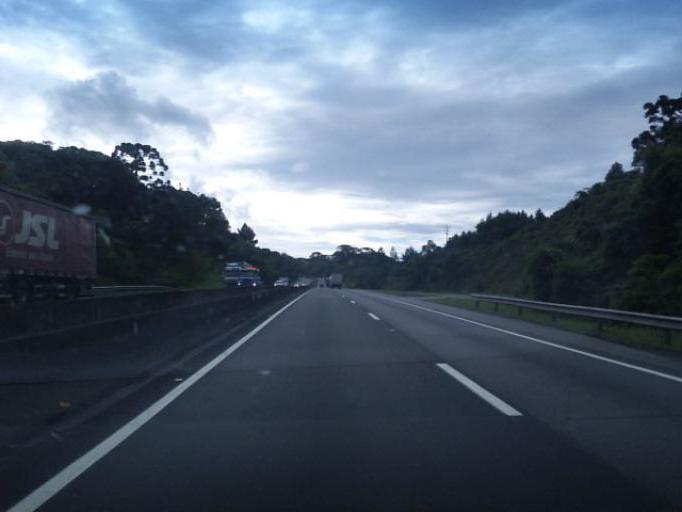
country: BR
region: Parana
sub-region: Campina Grande Do Sul
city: Campina Grande do Sul
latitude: -25.3069
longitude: -48.9888
